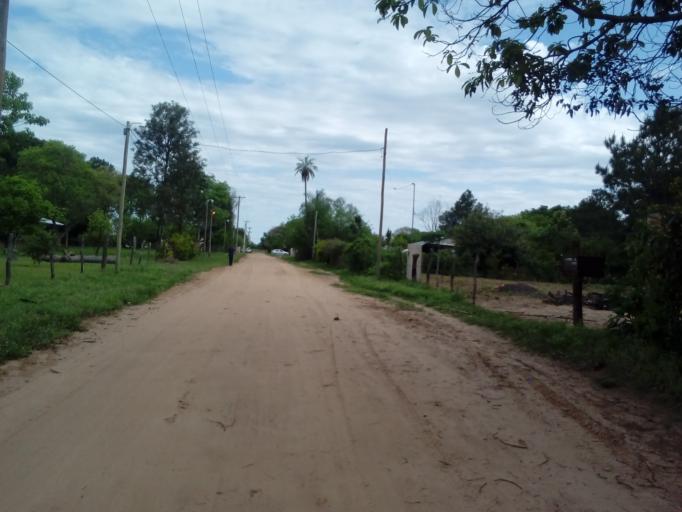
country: AR
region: Corrientes
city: San Luis del Palmar
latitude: -27.4602
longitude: -58.6525
